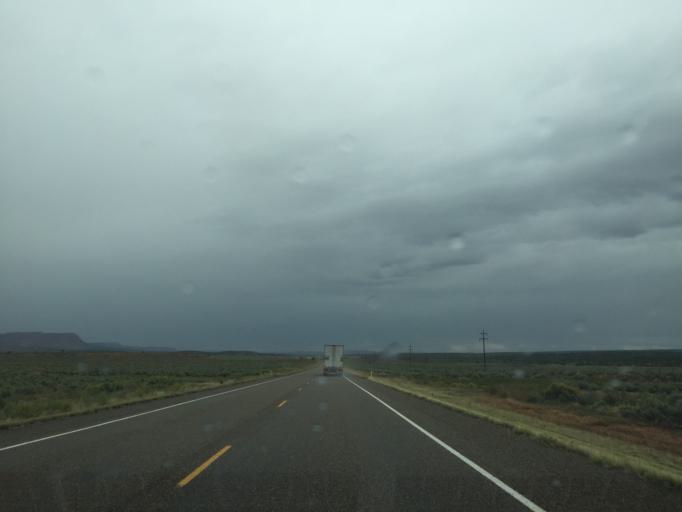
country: US
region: Utah
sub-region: Kane County
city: Kanab
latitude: 37.1144
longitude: -112.1124
